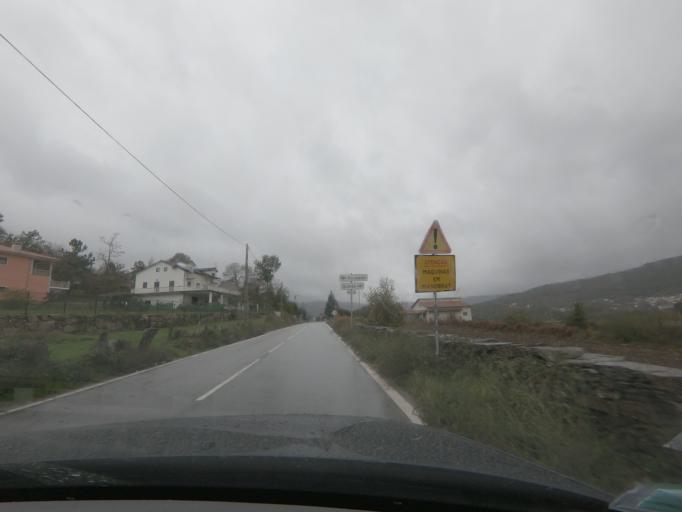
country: PT
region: Vila Real
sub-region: Santa Marta de Penaguiao
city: Santa Marta de Penaguiao
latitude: 41.2828
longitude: -7.8562
